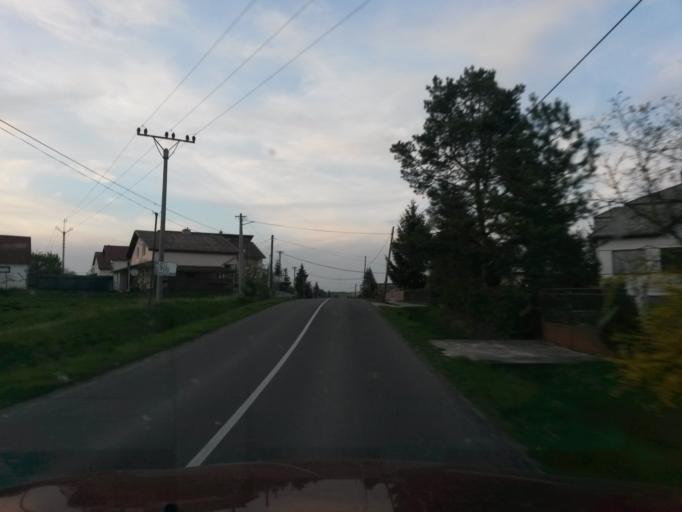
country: SK
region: Kosicky
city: Secovce
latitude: 48.5692
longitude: 21.5661
